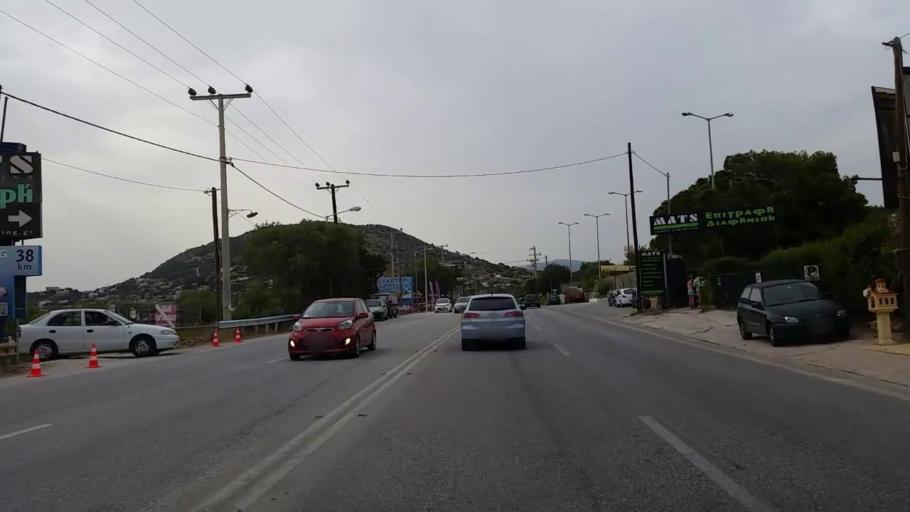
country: GR
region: Attica
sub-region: Nomarchia Anatolikis Attikis
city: Agios Dimitrios Kropias
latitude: 37.7970
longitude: 23.8716
